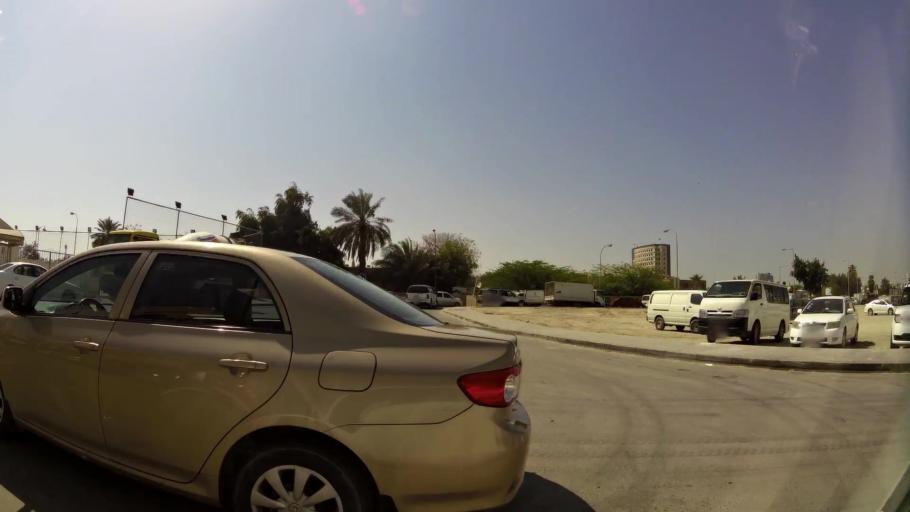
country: BH
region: Manama
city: Manama
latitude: 26.2099
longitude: 50.6008
